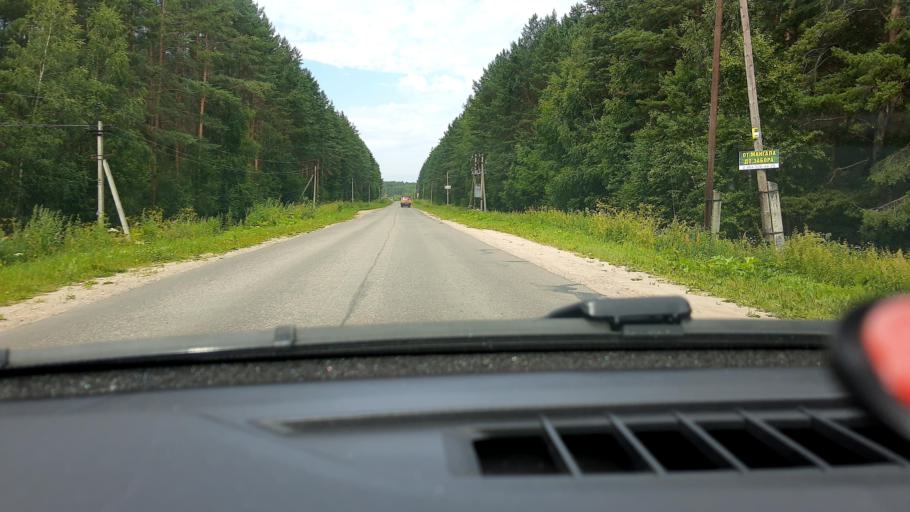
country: RU
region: Nizjnij Novgorod
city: Bogorodsk
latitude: 56.1304
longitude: 43.5936
